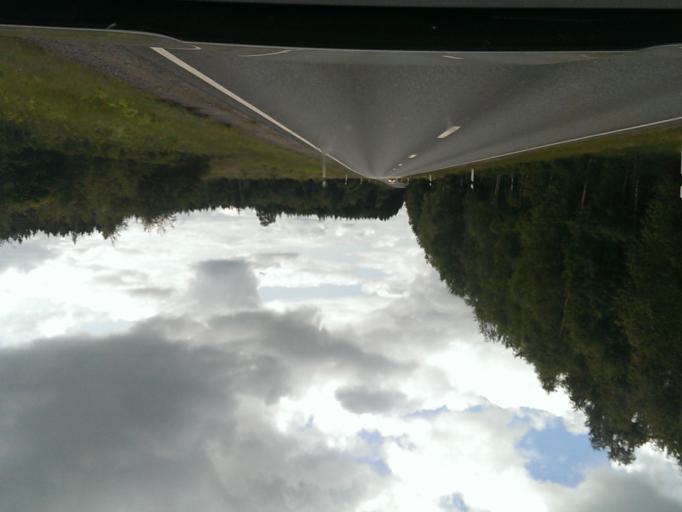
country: SE
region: Joenkoeping
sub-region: Varnamo Kommun
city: Varnamo
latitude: 57.2200
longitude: 14.0133
